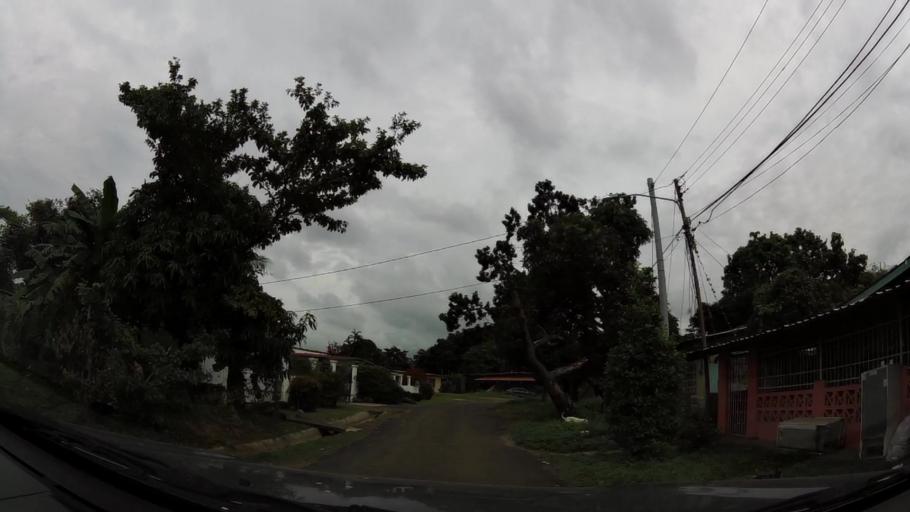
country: PA
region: Panama
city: San Miguelito
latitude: 9.0490
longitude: -79.4275
